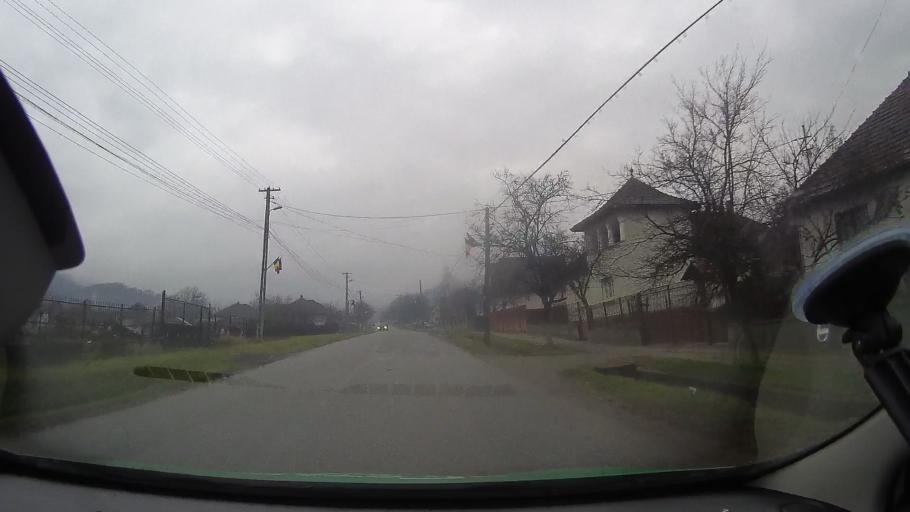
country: RO
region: Arad
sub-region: Comuna Gurahont
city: Gurahont
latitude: 46.2729
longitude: 22.3368
